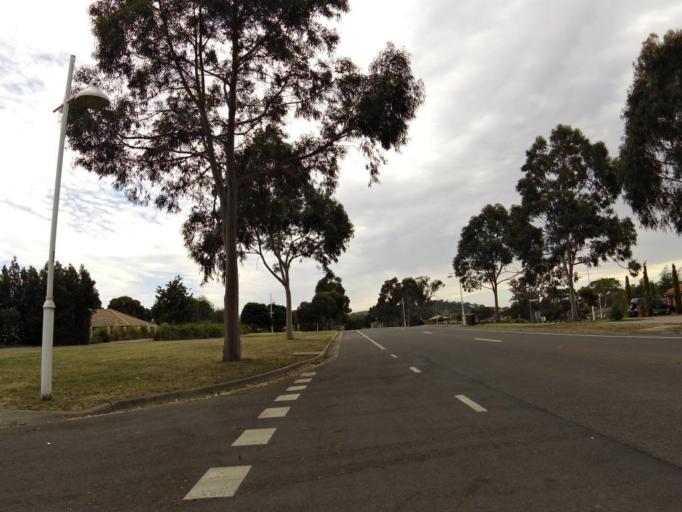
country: AU
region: Victoria
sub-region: Whittlesea
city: Mill Park
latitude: -37.6376
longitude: 145.0767
